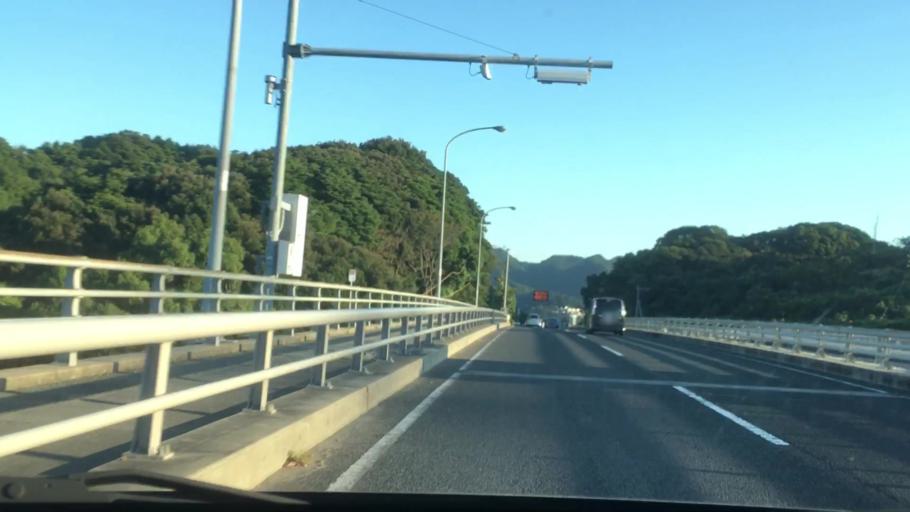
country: JP
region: Nagasaki
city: Sasebo
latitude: 33.1252
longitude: 129.7898
